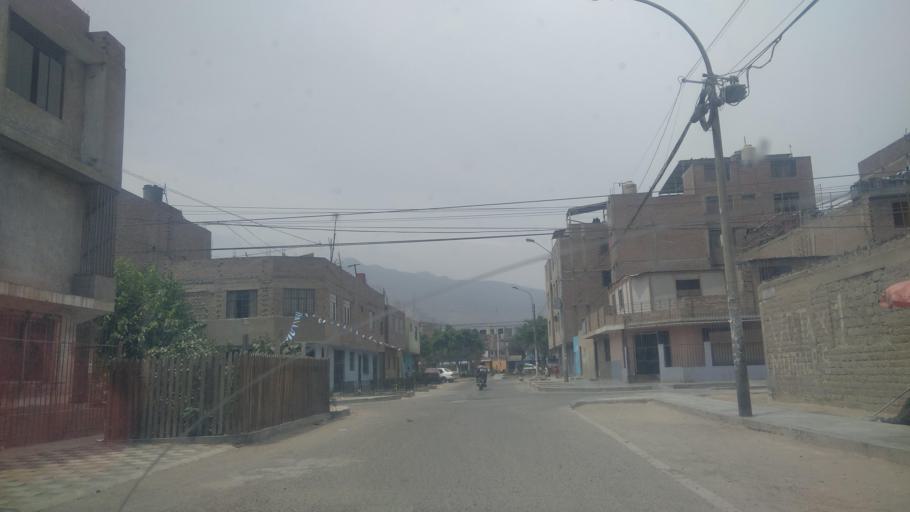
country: PE
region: Lima
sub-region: Lima
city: Independencia
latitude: -11.9865
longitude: -77.0137
